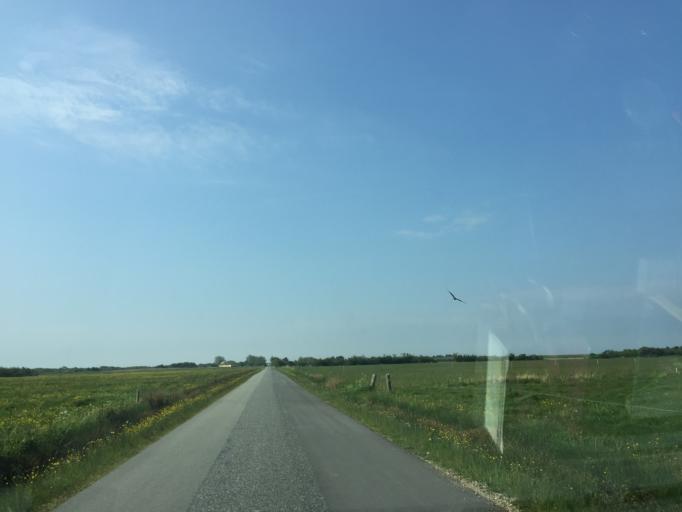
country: DK
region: South Denmark
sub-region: Esbjerg Kommune
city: Tjaereborg
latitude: 55.2855
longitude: 8.5579
